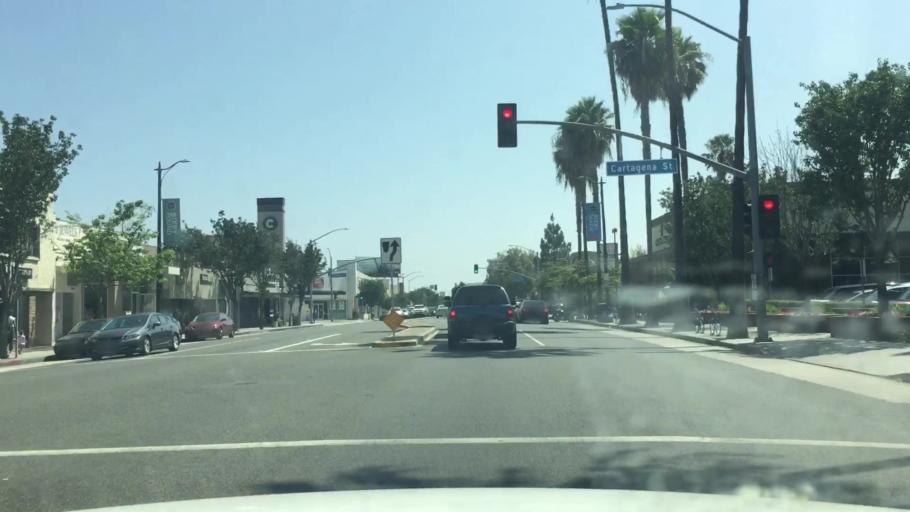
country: US
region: California
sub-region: Los Angeles County
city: Signal Hill
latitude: 33.8328
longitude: -118.1851
